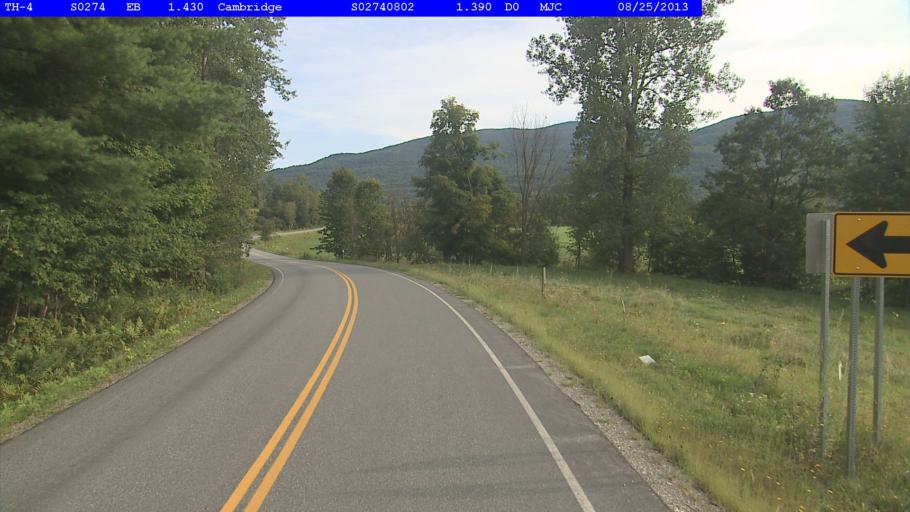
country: US
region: Vermont
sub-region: Lamoille County
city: Johnson
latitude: 44.6652
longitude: -72.7601
